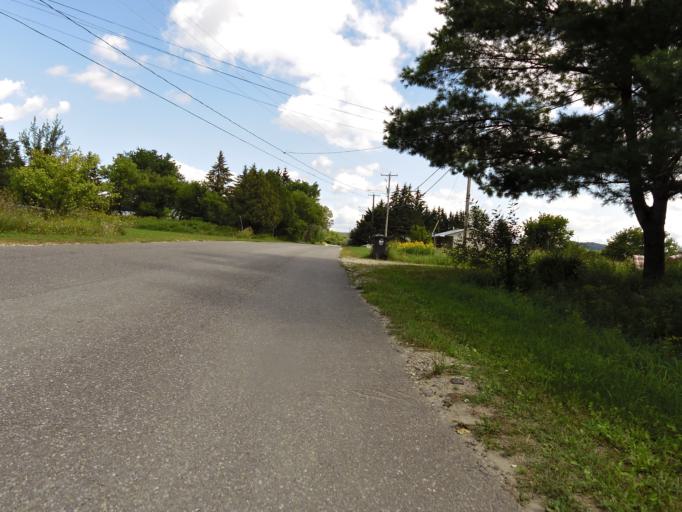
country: CA
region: Quebec
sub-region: Outaouais
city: Wakefield
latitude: 45.8109
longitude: -75.9609
